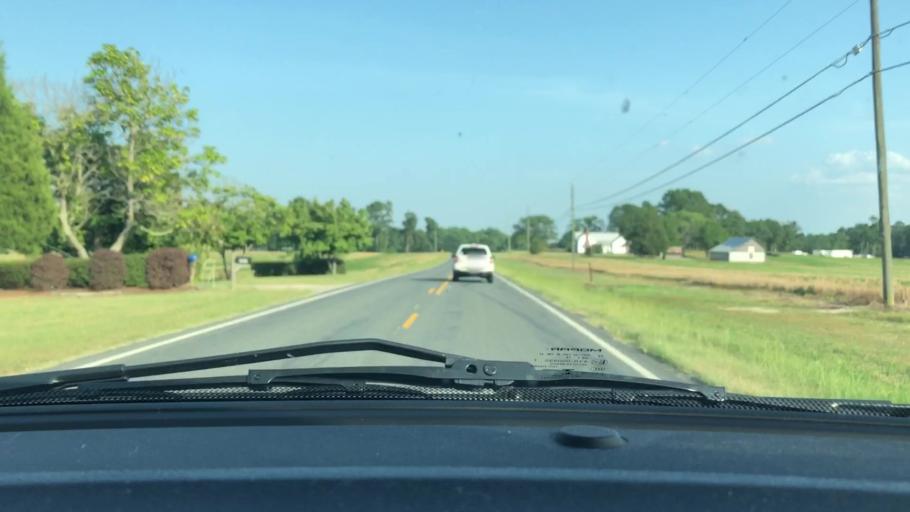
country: US
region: North Carolina
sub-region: Lee County
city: Broadway
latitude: 35.3664
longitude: -79.0941
